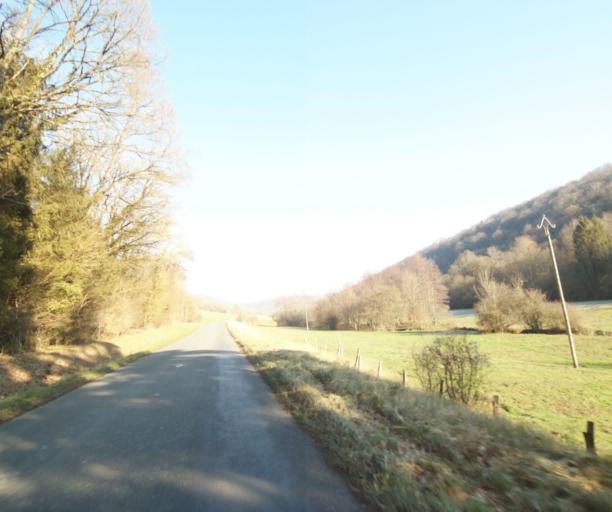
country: FR
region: Champagne-Ardenne
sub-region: Departement de la Haute-Marne
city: Chevillon
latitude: 48.4990
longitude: 5.1552
